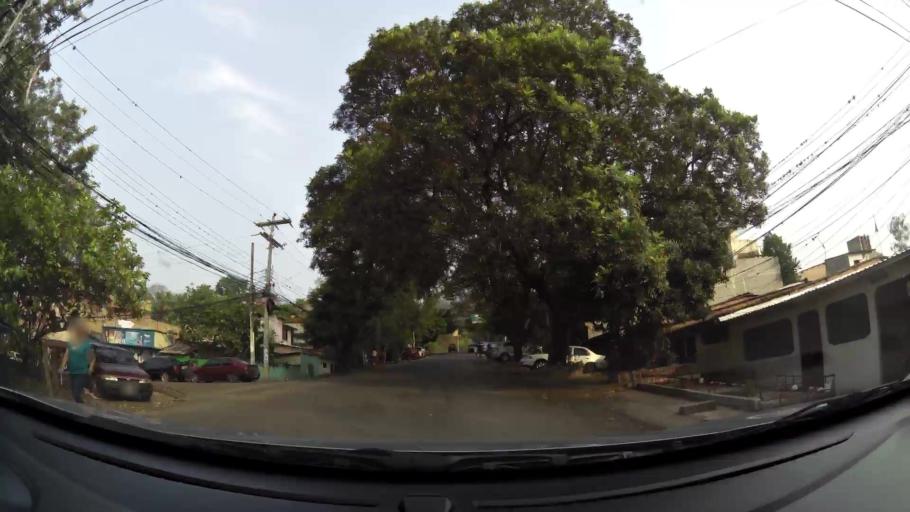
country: HN
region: Francisco Morazan
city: Tegucigalpa
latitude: 14.0679
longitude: -87.1766
